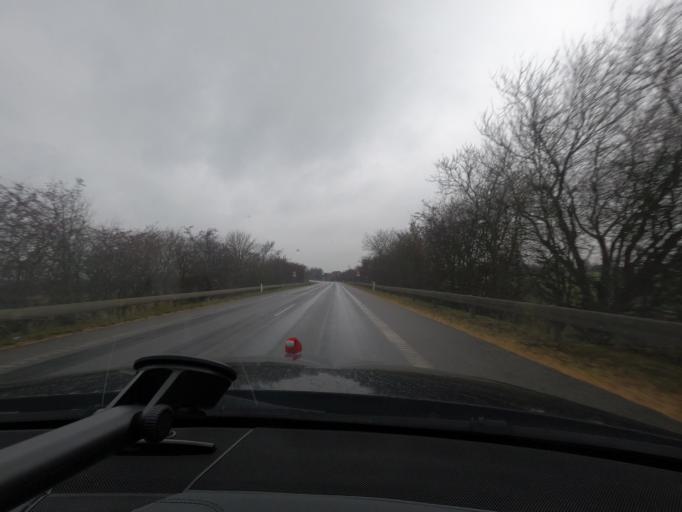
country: DK
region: South Denmark
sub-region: Sonderborg Kommune
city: Horuphav
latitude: 54.8929
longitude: 9.9700
